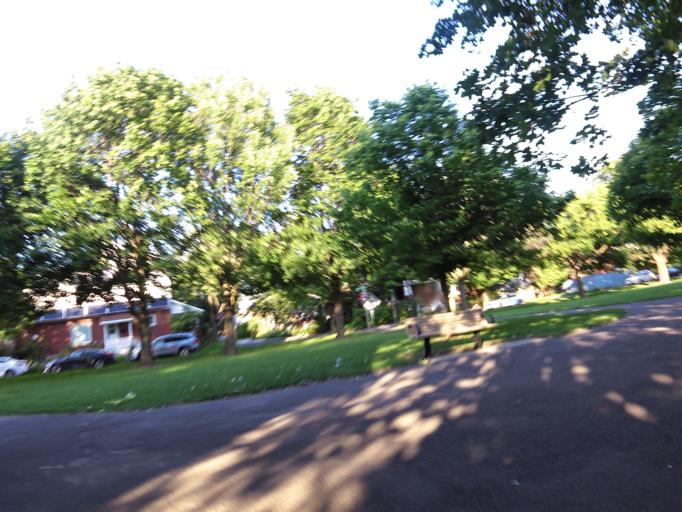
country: CA
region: Ontario
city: Ottawa
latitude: 45.3891
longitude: -75.6886
